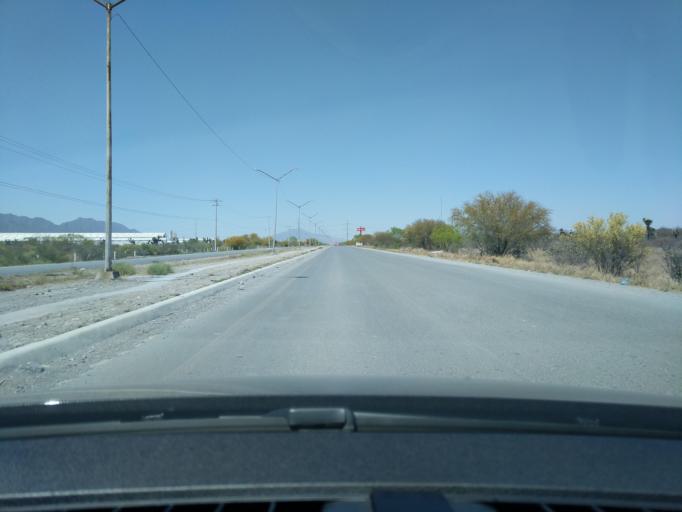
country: MX
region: Nuevo Leon
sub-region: Salinas Victoria
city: Emiliano Zapata
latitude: 25.9212
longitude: -100.2711
